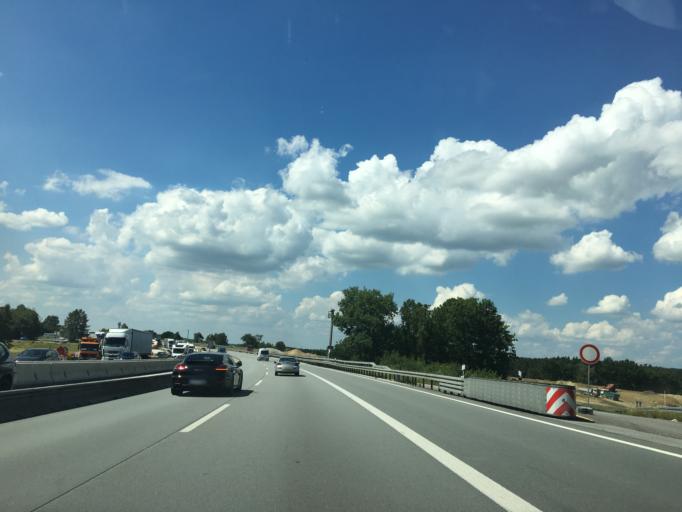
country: DE
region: Bavaria
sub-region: Upper Bavaria
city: Wolnzach
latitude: 48.5784
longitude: 11.5919
